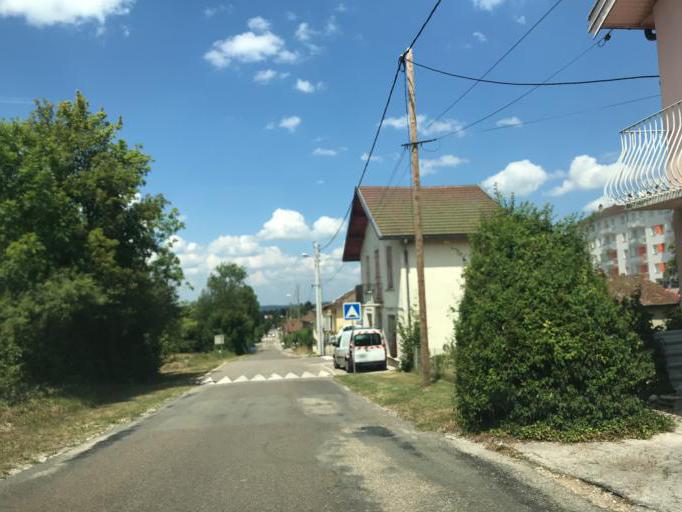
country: FR
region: Franche-Comte
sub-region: Departement du Jura
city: Clairvaux-les-Lacs
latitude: 46.5699
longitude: 5.7569
